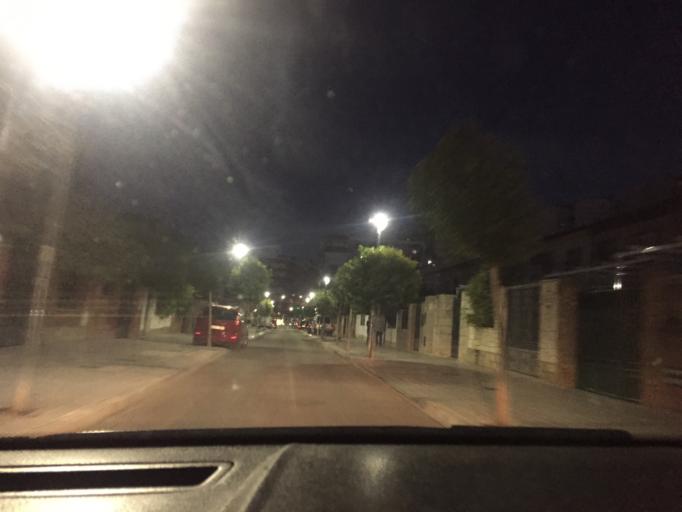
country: ES
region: Andalusia
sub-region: Provincia de Jaen
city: Jaen
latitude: 37.7787
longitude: -3.7946
